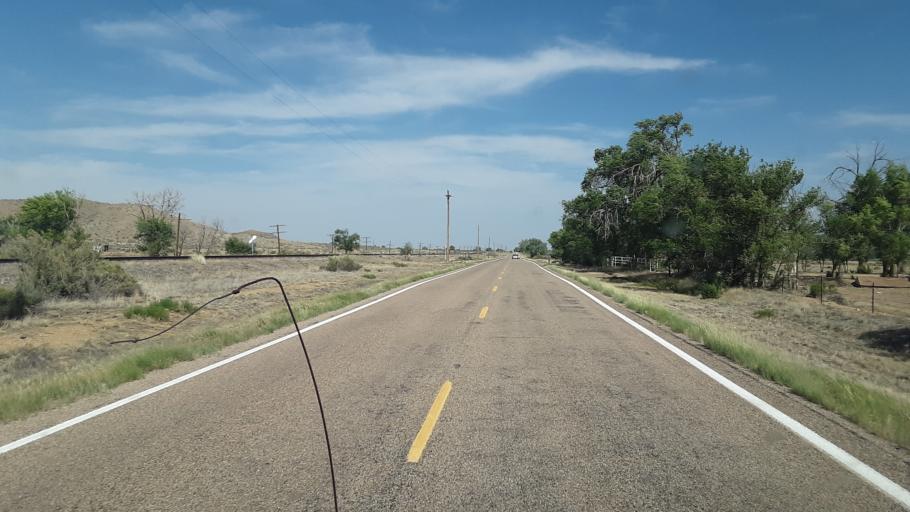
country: US
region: Colorado
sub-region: Otero County
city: Fowler
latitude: 38.1619
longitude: -104.0491
